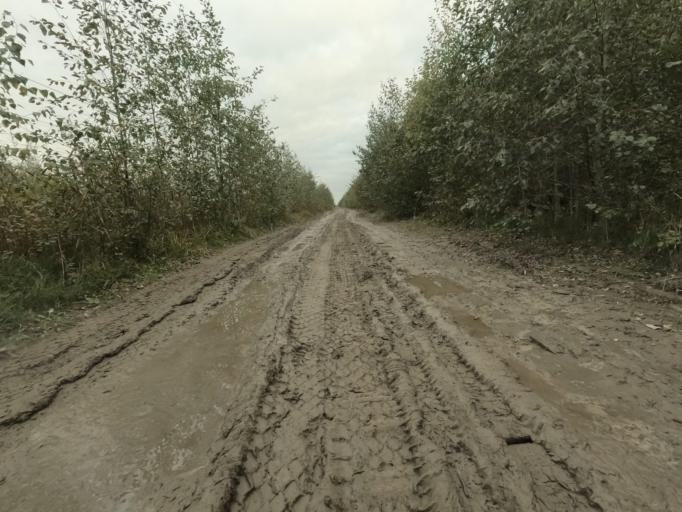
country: RU
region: St.-Petersburg
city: Sapernyy
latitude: 59.7542
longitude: 30.6975
